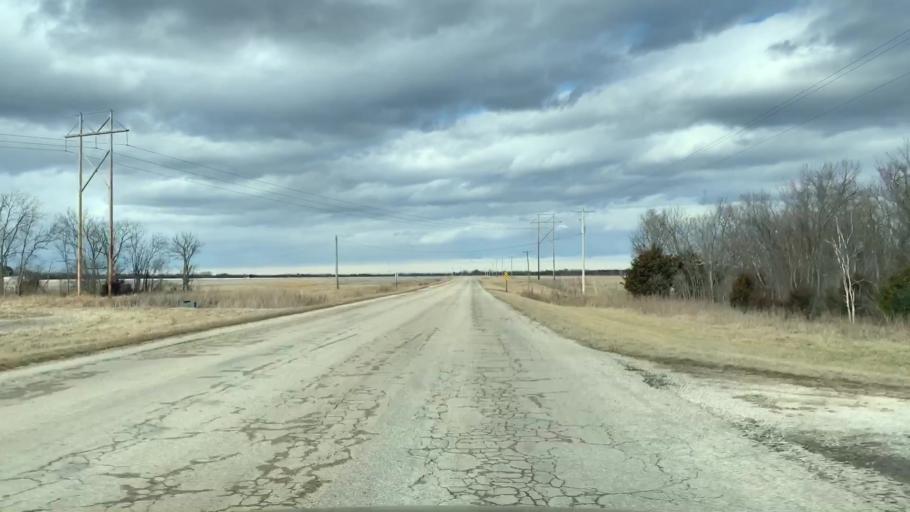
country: US
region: Kansas
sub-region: Allen County
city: Humboldt
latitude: 37.7687
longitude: -95.4706
